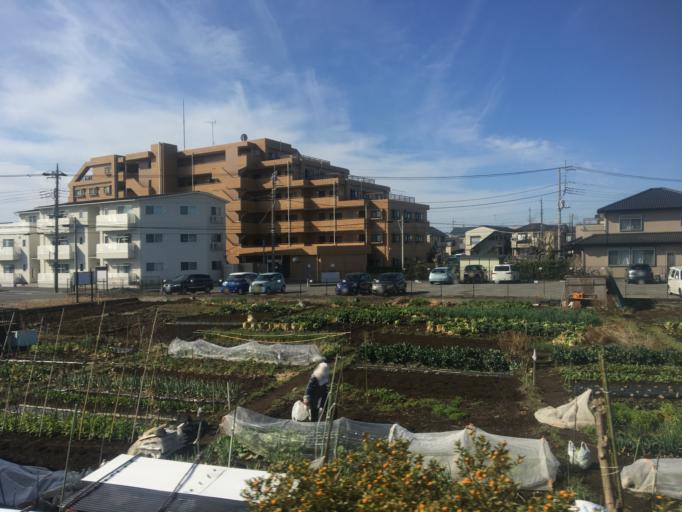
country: JP
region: Saitama
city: Sakado
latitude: 35.9408
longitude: 139.4186
